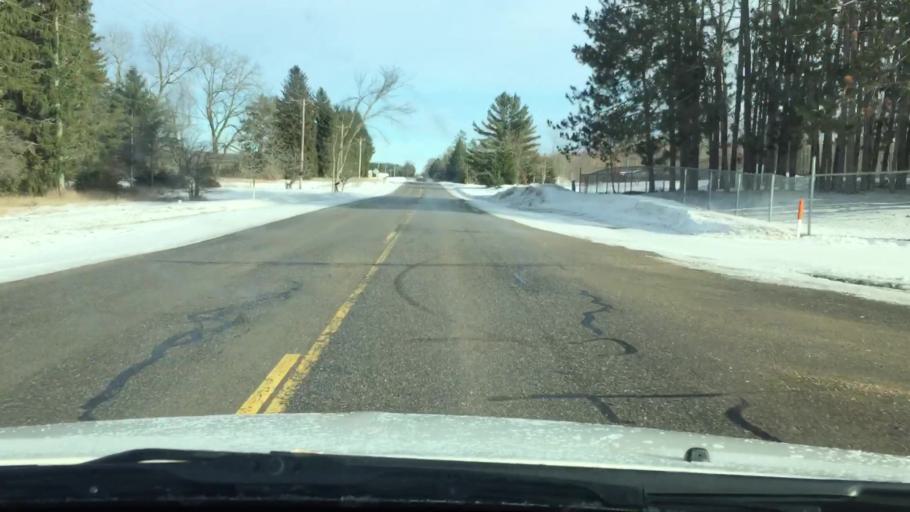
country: US
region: Michigan
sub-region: Kalkaska County
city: Kalkaska
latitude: 44.6408
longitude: -85.2509
